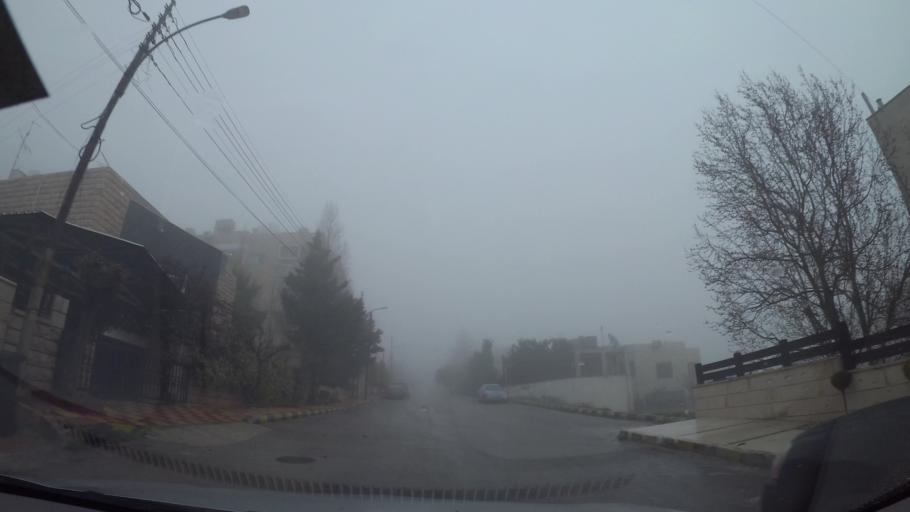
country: JO
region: Amman
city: Al Jubayhah
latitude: 32.0094
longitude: 35.8803
